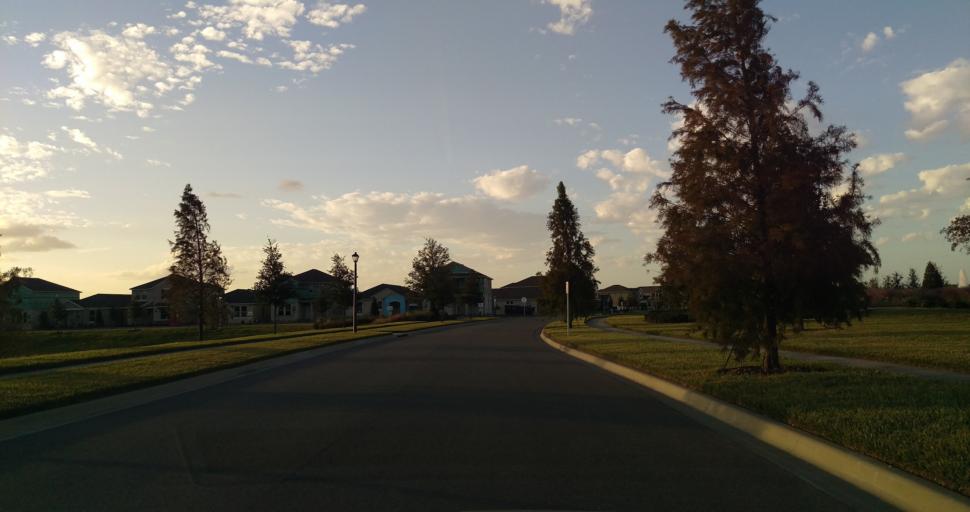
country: US
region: Florida
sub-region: Polk County
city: Citrus Ridge
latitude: 28.4317
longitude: -81.6371
